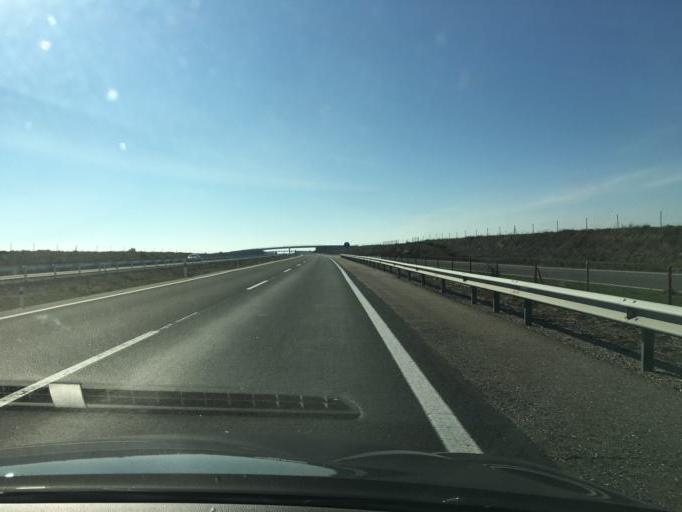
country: ES
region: Castille and Leon
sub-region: Provincia de Burgos
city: Grisalena
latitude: 42.5755
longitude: -3.2568
